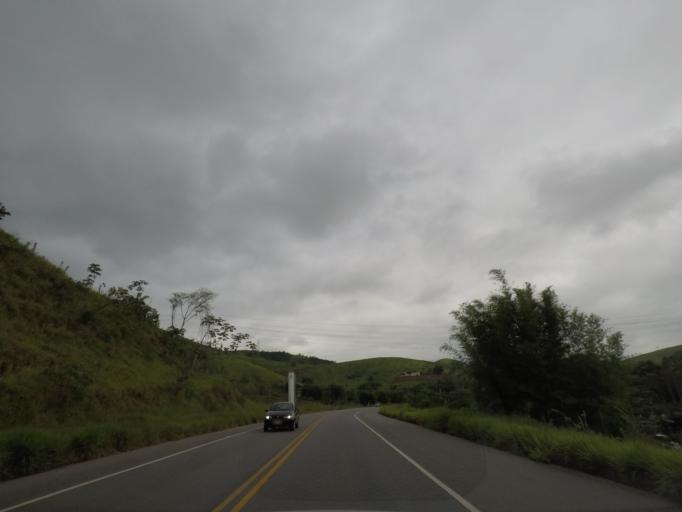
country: BR
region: Sao Paulo
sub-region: Guaratingueta
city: Guaratingueta
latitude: -22.8610
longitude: -45.1791
